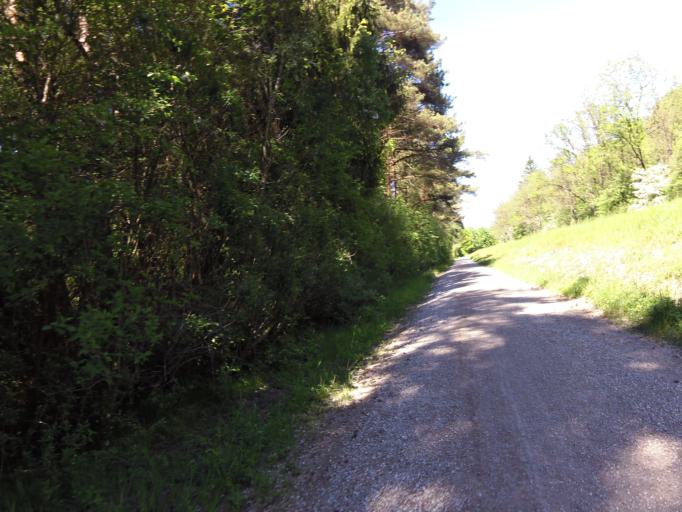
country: DE
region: Bavaria
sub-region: Upper Bavaria
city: Moosburg
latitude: 48.4427
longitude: 11.9263
